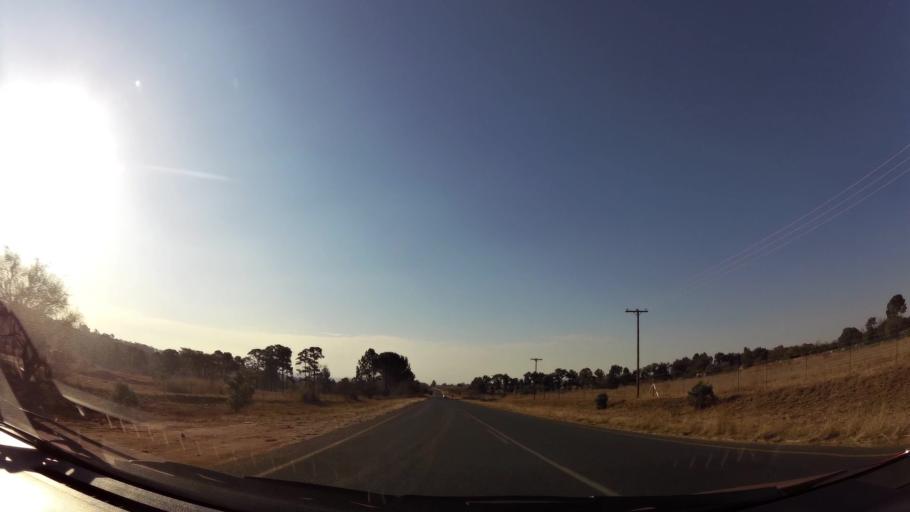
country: ZA
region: Gauteng
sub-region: West Rand District Municipality
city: Muldersdriseloop
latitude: -26.0186
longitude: 27.9092
